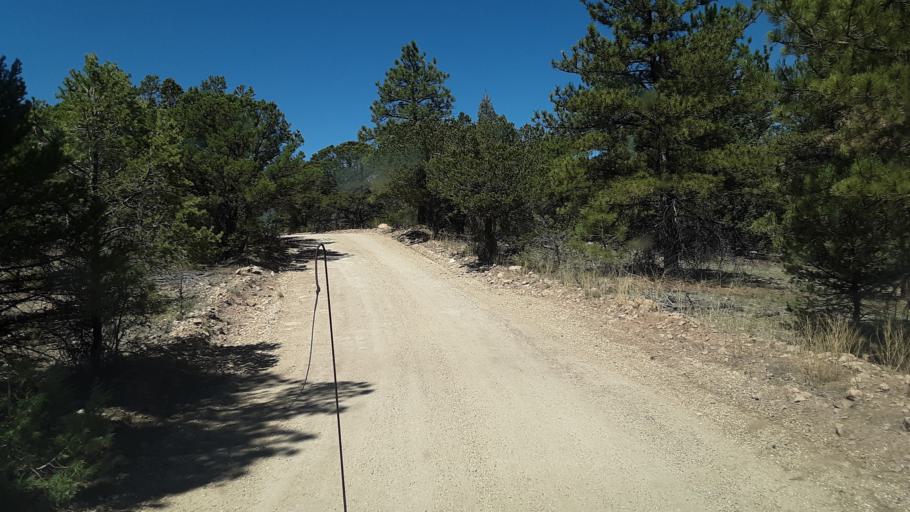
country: US
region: Colorado
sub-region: Custer County
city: Westcliffe
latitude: 38.2527
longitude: -105.5648
